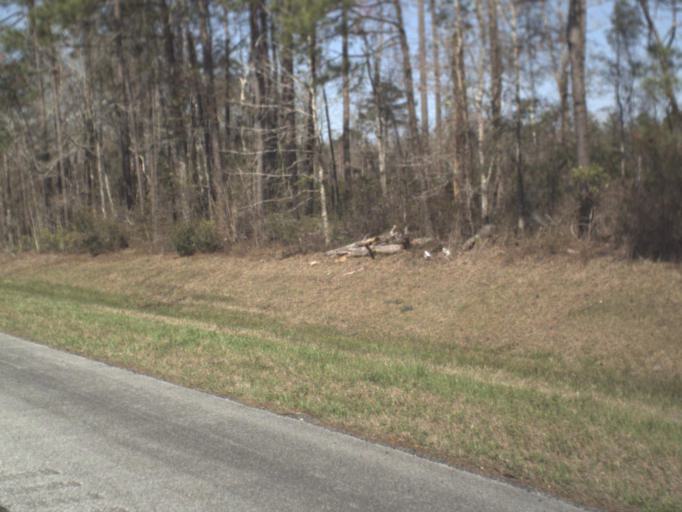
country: US
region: Florida
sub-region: Jackson County
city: Sneads
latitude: 30.6362
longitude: -84.9336
